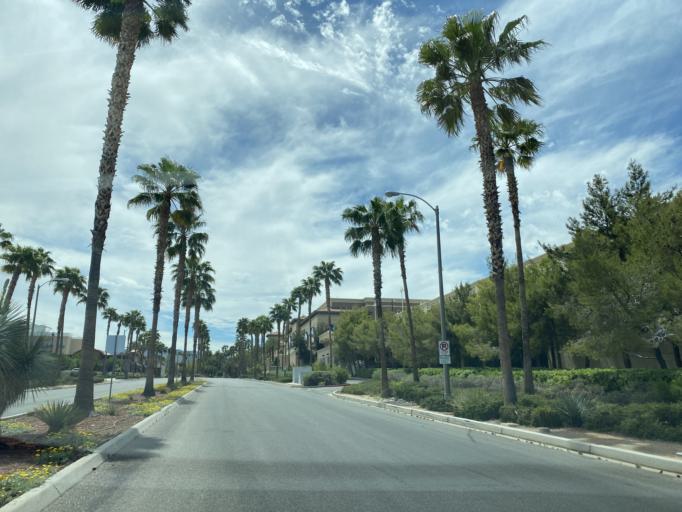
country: US
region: Nevada
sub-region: Clark County
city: Whitney
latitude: 36.0229
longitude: -115.0891
